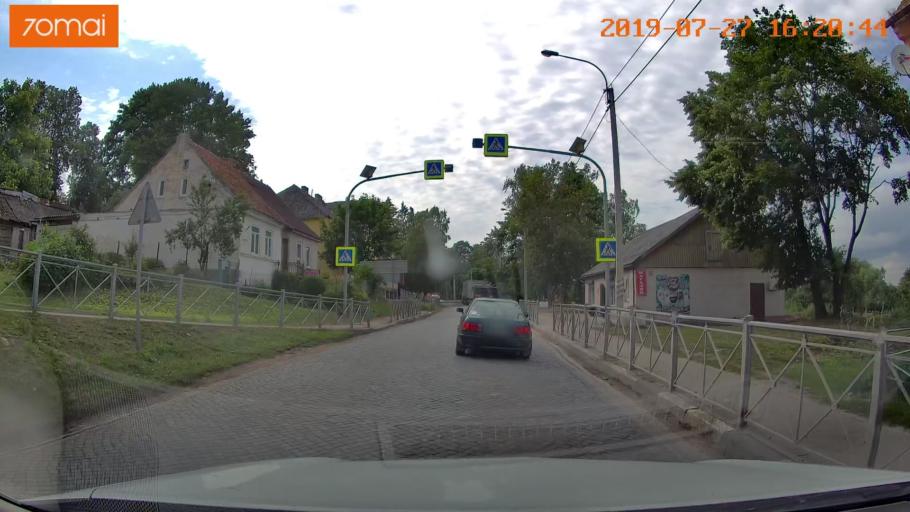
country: RU
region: Kaliningrad
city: Chernyakhovsk
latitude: 54.6263
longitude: 21.5229
